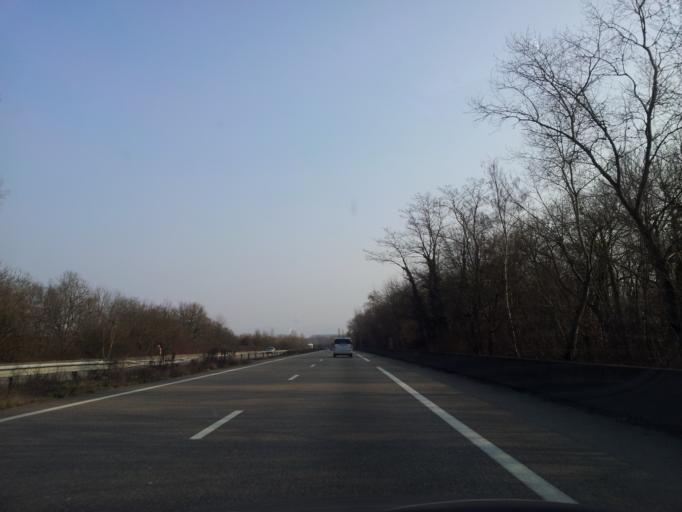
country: FR
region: Alsace
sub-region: Departement du Haut-Rhin
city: Blotzheim
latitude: 47.6182
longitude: 7.5142
